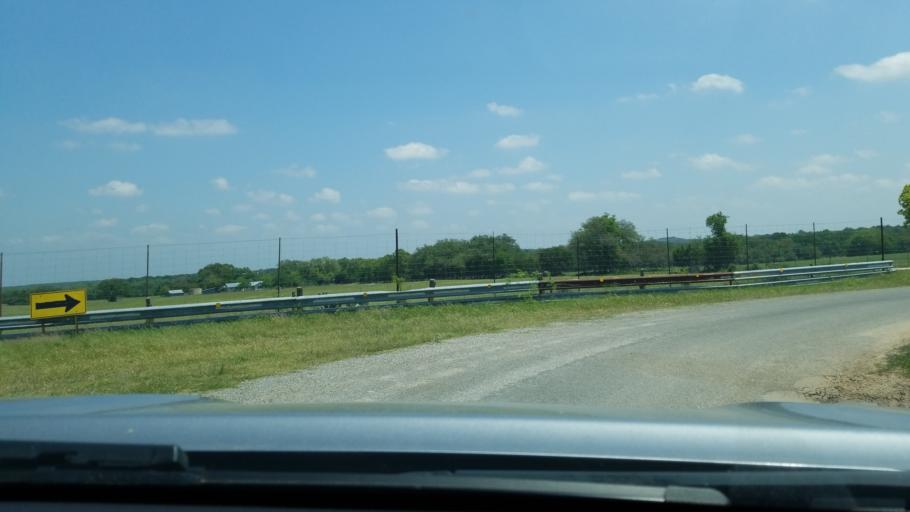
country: US
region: Texas
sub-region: Blanco County
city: Blanco
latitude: 30.0761
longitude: -98.3963
